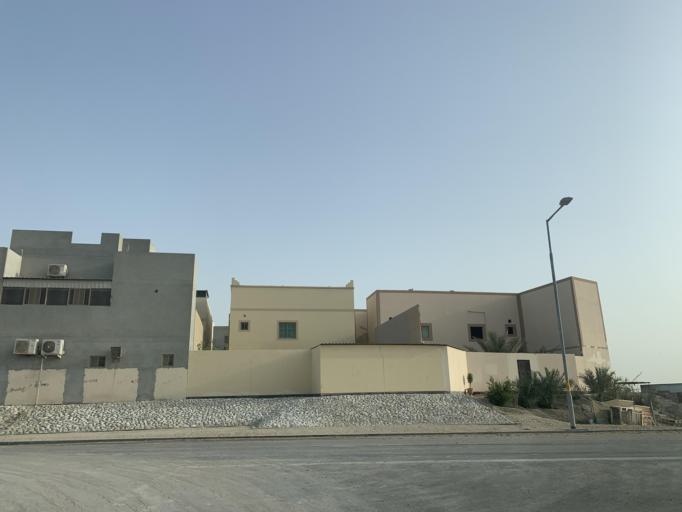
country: BH
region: Northern
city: Madinat `Isa
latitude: 26.1644
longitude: 50.5090
